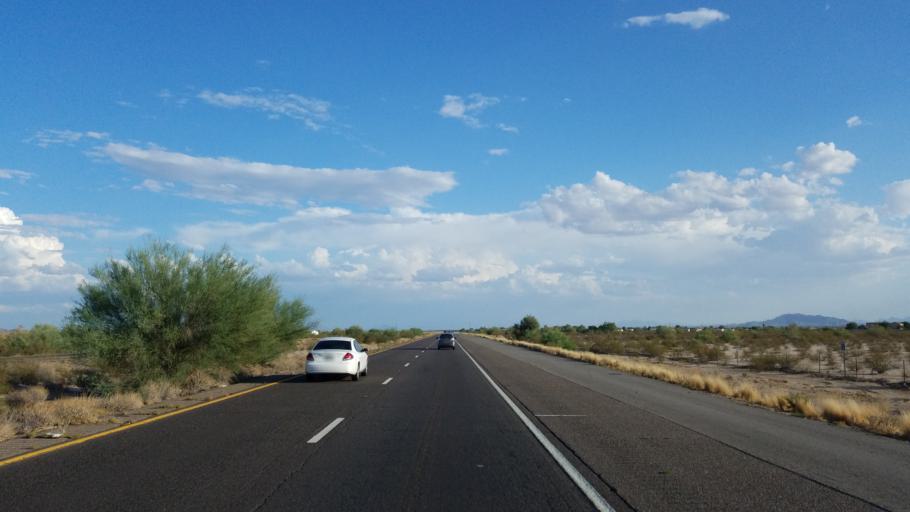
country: US
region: Arizona
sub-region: Pinal County
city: Sacaton
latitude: 32.9887
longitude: -111.7417
